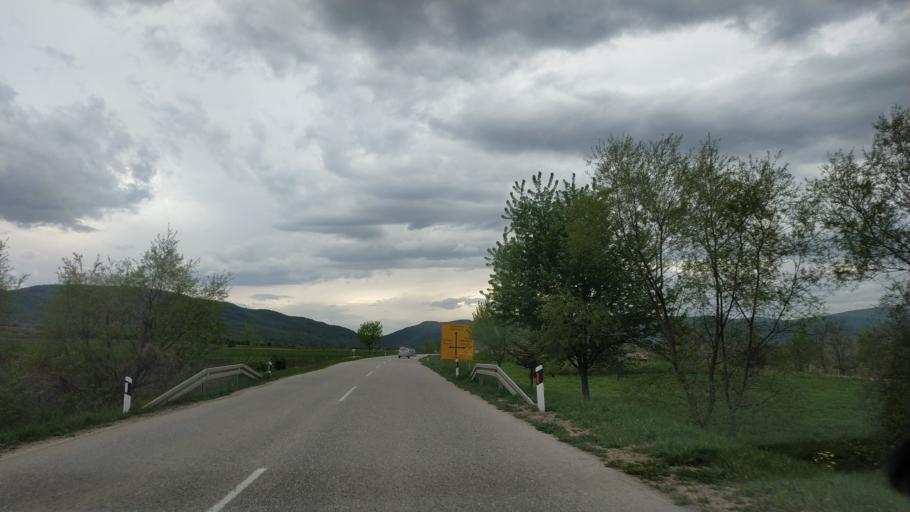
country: RS
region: Central Serbia
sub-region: Zajecarski Okrug
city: Soko Banja
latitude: 43.6566
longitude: 21.8084
